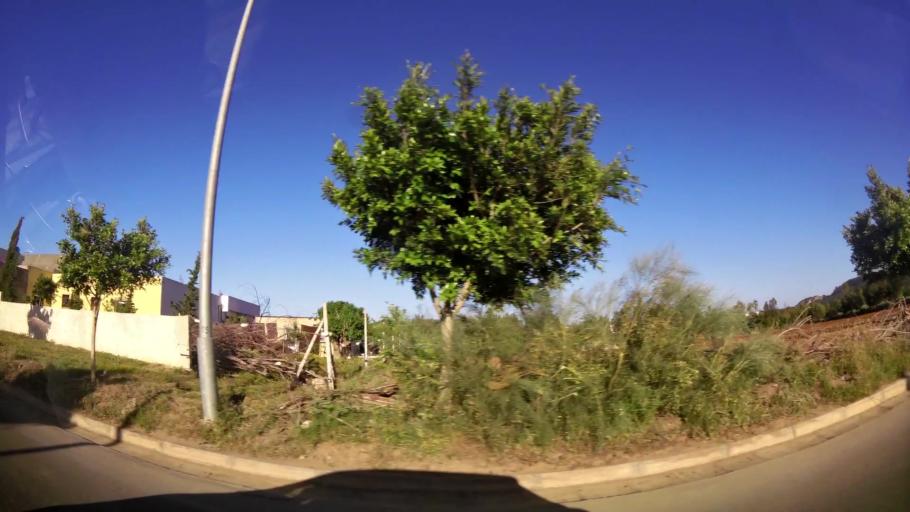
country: MA
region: Oriental
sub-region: Berkane-Taourirt
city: Madagh
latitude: 35.0791
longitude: -2.2446
